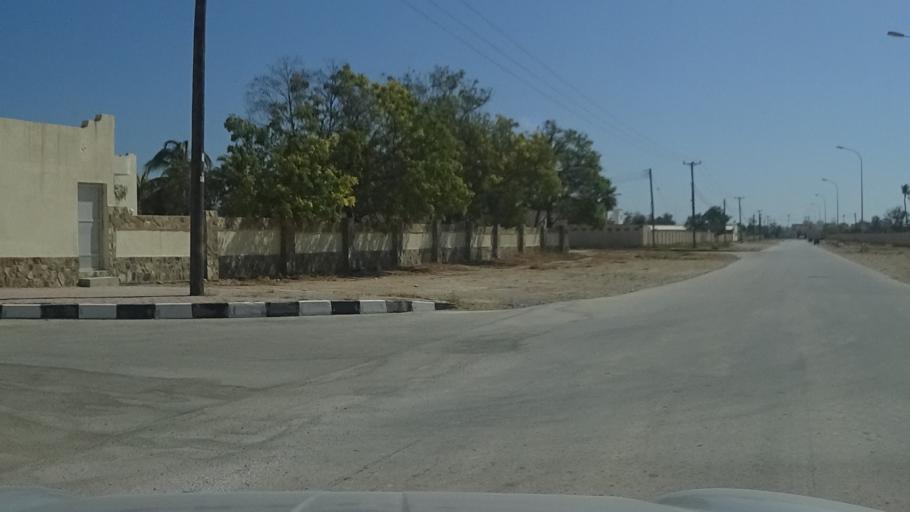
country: OM
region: Zufar
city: Salalah
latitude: 17.0302
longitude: 54.1666
